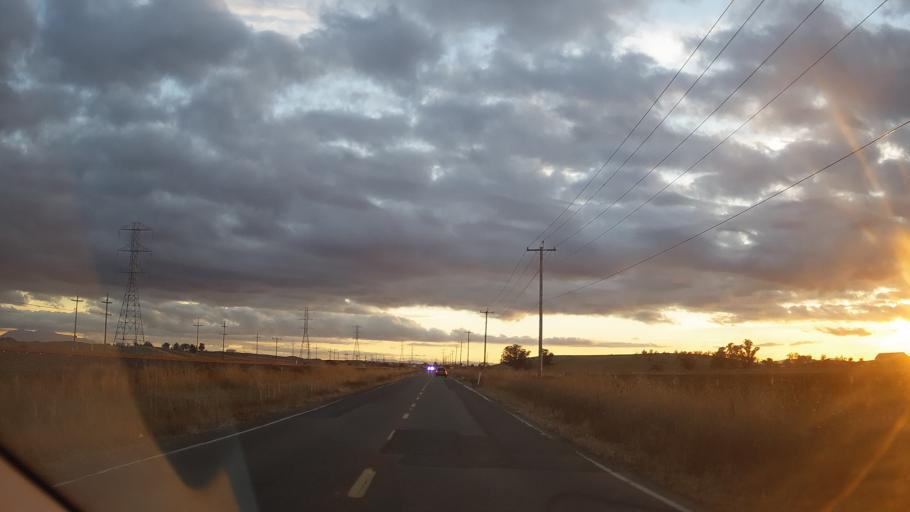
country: US
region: California
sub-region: Solano County
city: Vacaville
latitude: 38.3095
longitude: -121.9446
